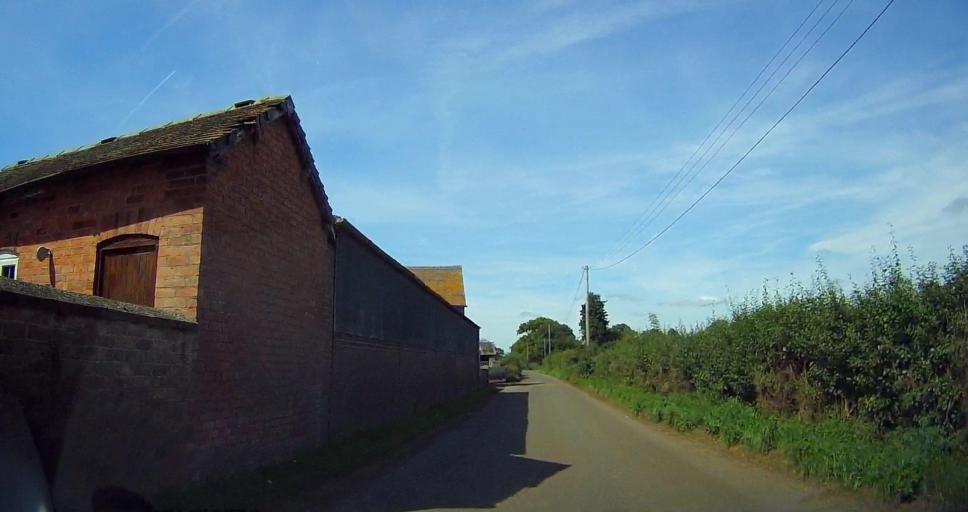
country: GB
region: England
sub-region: Cheshire East
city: Nantwich
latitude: 52.9882
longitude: -2.5334
